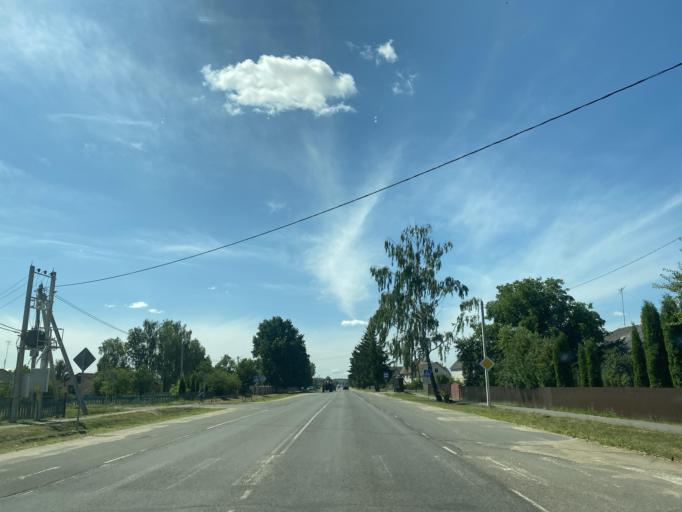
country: BY
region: Brest
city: Ivanava
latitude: 52.1615
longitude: 25.5465
